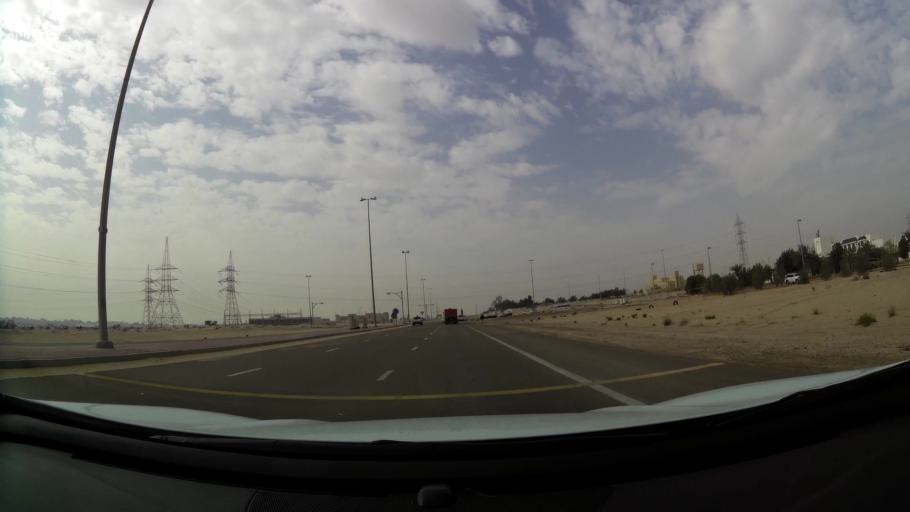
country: AE
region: Abu Dhabi
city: Abu Dhabi
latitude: 24.2974
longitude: 54.6627
